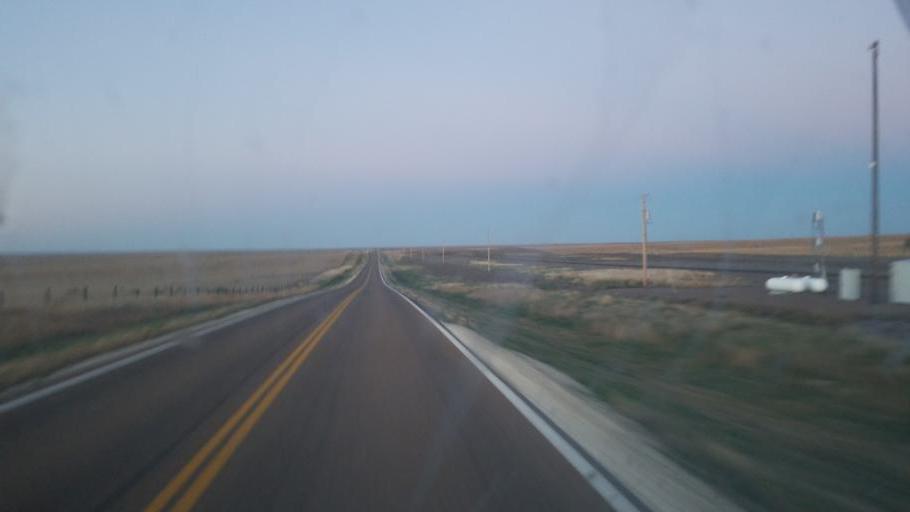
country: US
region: Kansas
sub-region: Wallace County
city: Sharon Springs
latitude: 38.9788
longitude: -101.4323
